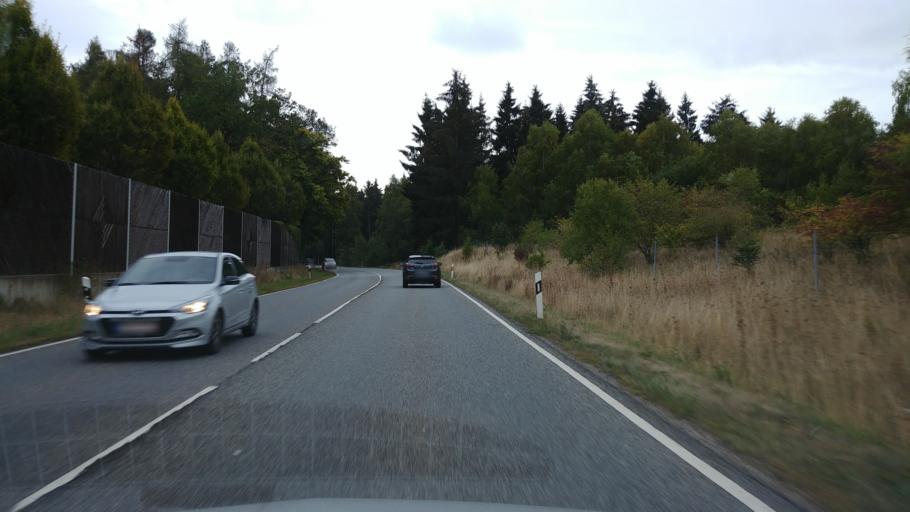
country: DE
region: Hesse
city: Taunusstein
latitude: 50.1512
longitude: 8.2130
